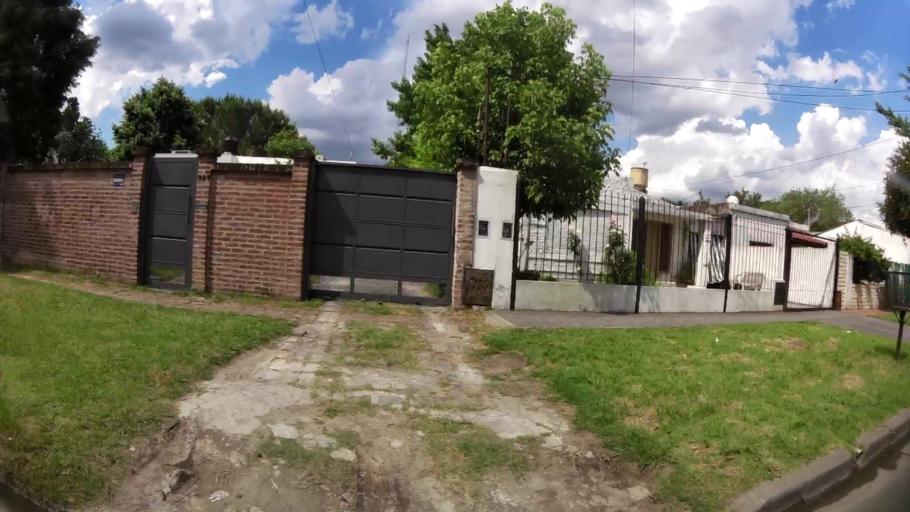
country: AR
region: Buenos Aires
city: Ituzaingo
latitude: -34.6408
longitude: -58.6709
